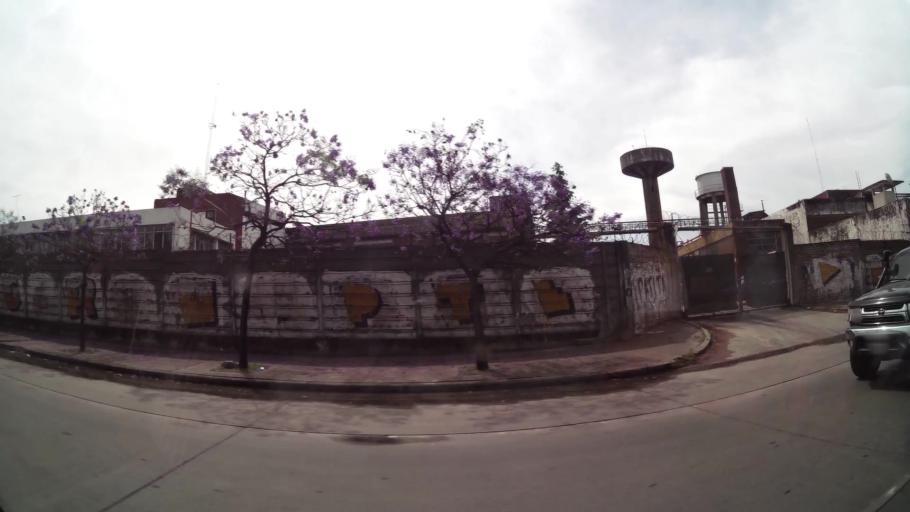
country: AR
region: Buenos Aires F.D.
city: Villa Lugano
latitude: -34.6643
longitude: -58.4272
